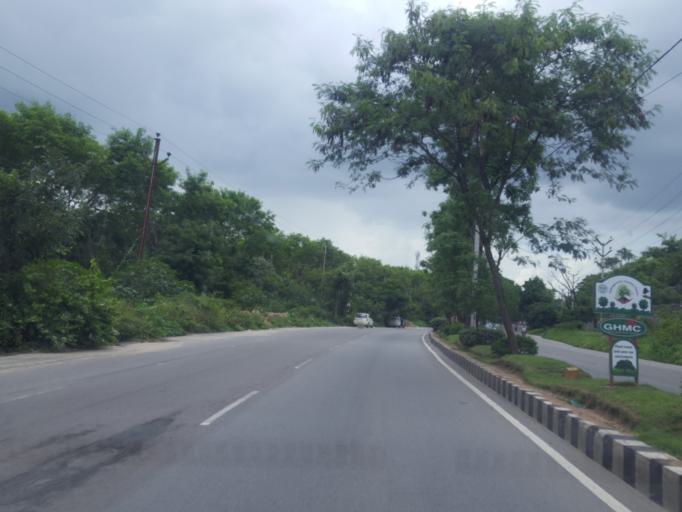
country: IN
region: Telangana
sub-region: Medak
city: Serilingampalle
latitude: 17.4518
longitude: 78.3445
